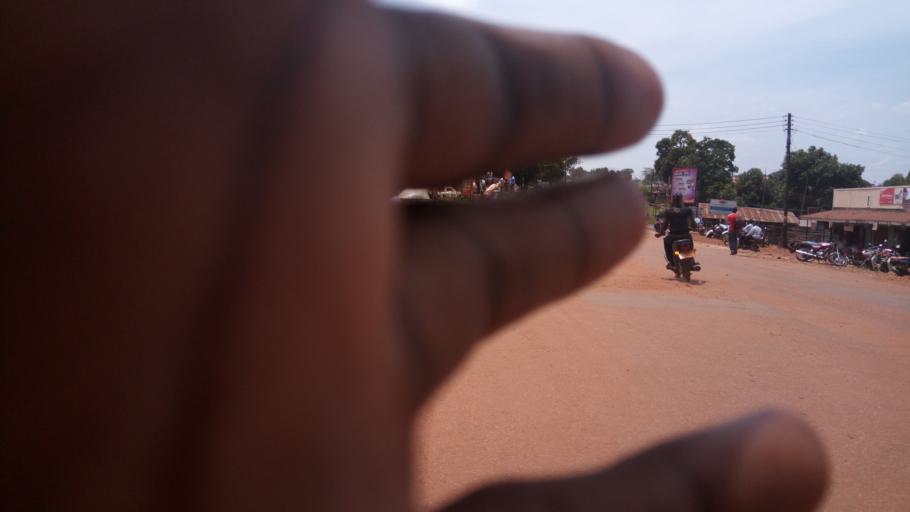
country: UG
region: Central Region
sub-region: Mityana District
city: Mityana
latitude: 0.3996
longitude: 32.0457
